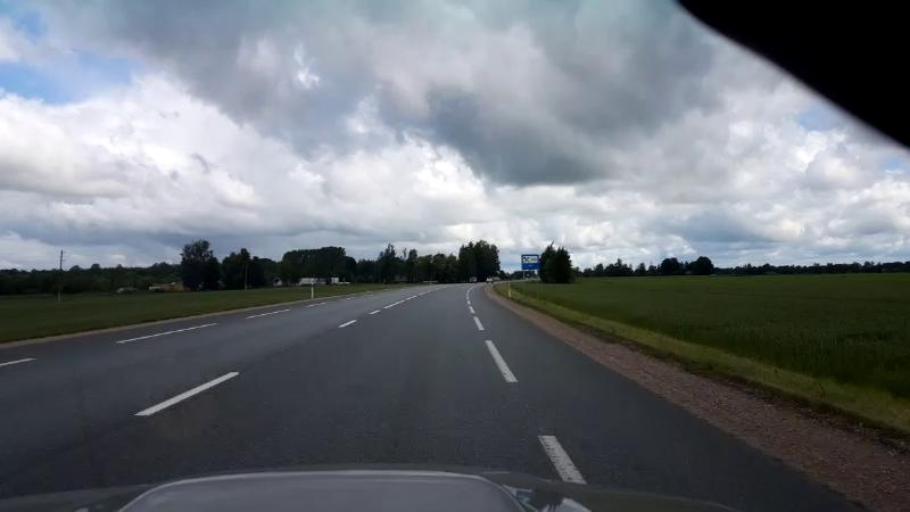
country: LV
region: Bauskas Rajons
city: Bauska
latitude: 56.4490
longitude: 24.1642
